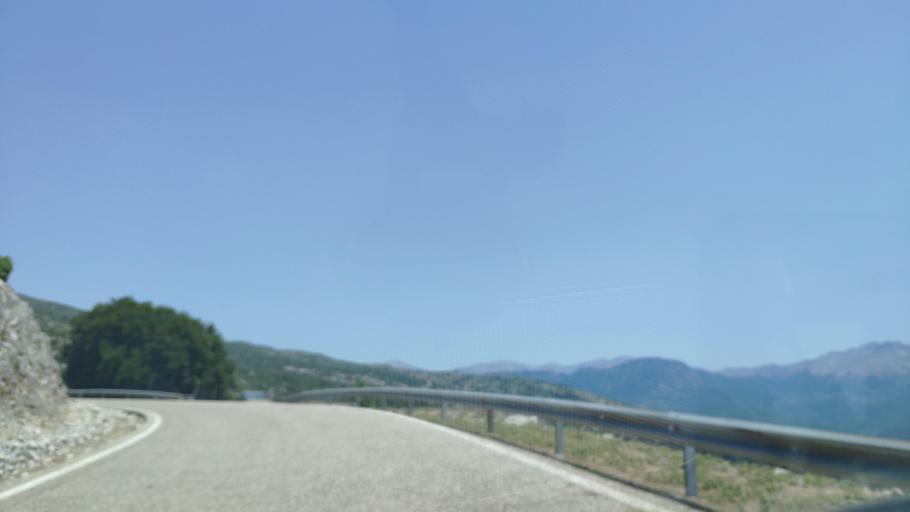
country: GR
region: West Greece
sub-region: Nomos Aitolias kai Akarnanias
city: Krikellos
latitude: 39.0635
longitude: 21.3823
